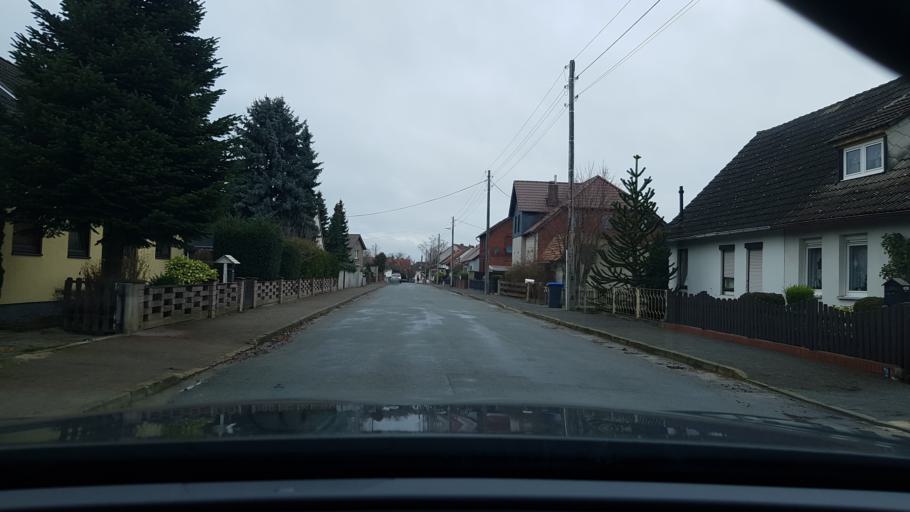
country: DE
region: Saxony-Anhalt
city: Weferlingen
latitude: 52.3980
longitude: 11.1158
